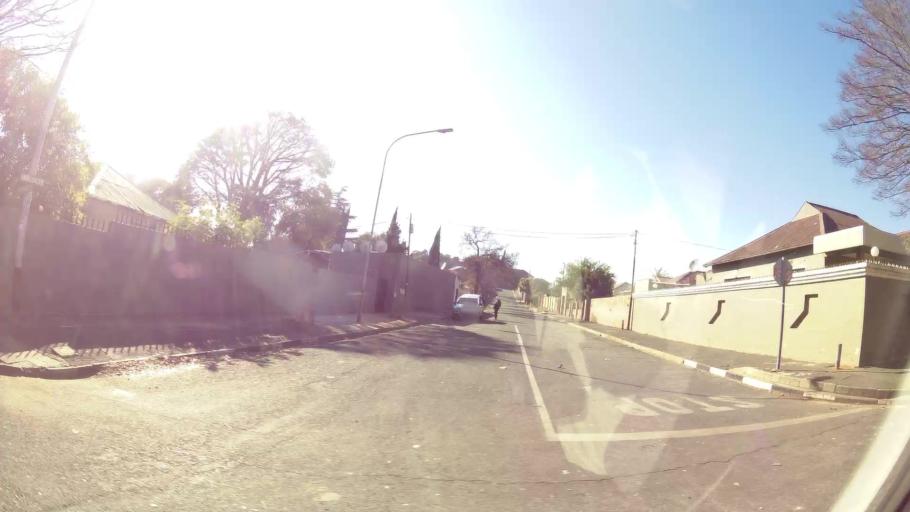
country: ZA
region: Gauteng
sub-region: City of Johannesburg Metropolitan Municipality
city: Johannesburg
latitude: -26.2016
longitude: 28.0982
